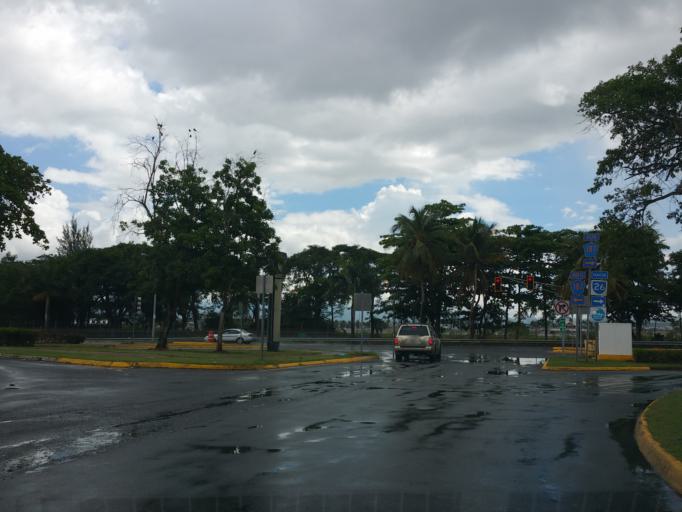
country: PR
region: Carolina
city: Carolina
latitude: 18.4418
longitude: -66.0146
